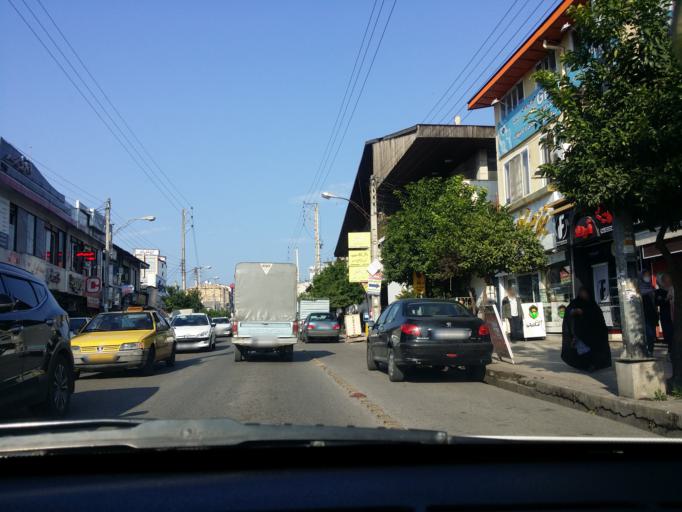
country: IR
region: Mazandaran
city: Chalus
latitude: 36.6558
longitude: 51.4190
